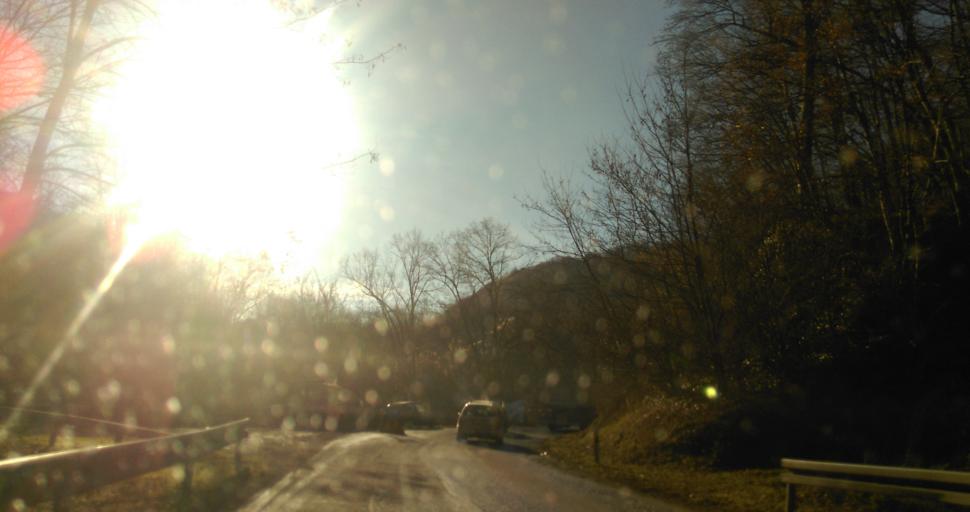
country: RS
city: Vrdnik
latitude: 45.1715
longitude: 19.8263
